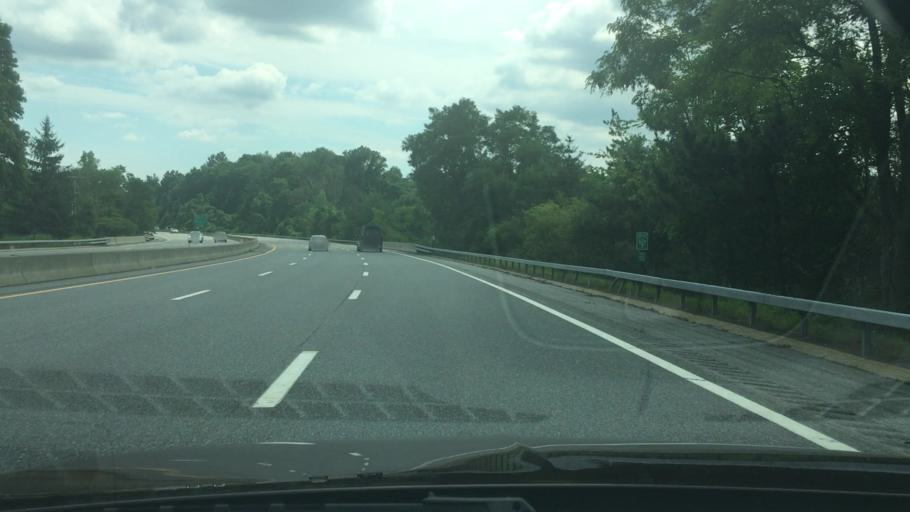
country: US
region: New York
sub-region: Westchester County
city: Briarcliff Manor
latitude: 41.1588
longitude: -73.8183
